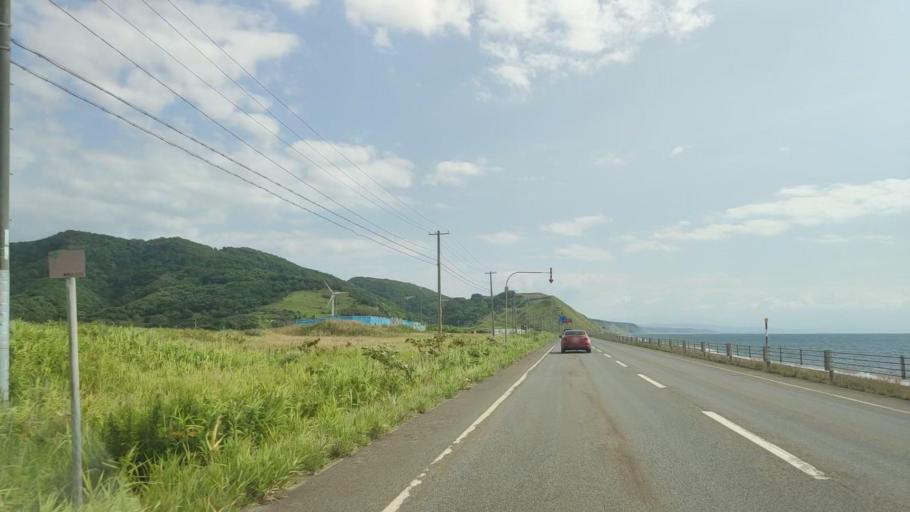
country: JP
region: Hokkaido
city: Rumoi
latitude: 44.0764
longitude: 141.6627
